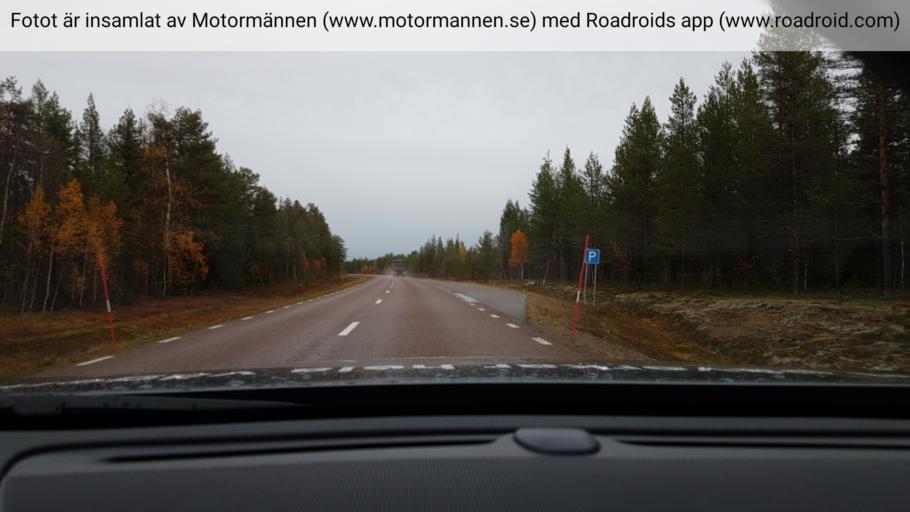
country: SE
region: Norrbotten
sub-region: Pajala Kommun
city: Pajala
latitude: 67.1707
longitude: 22.6768
